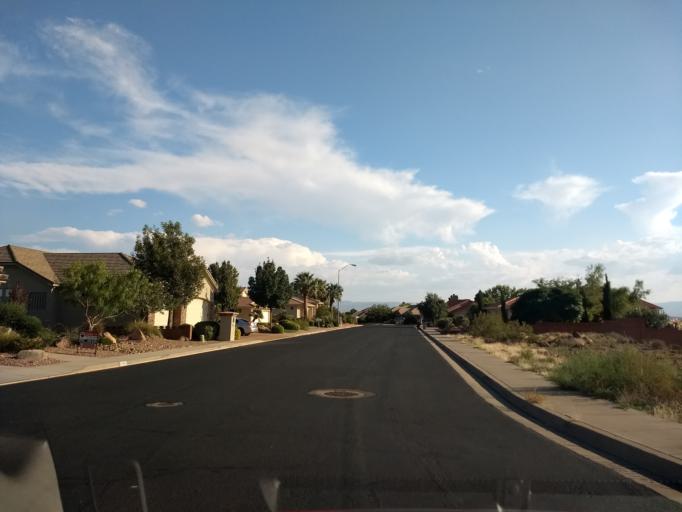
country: US
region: Utah
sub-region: Washington County
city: Saint George
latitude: 37.1129
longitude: -113.5512
